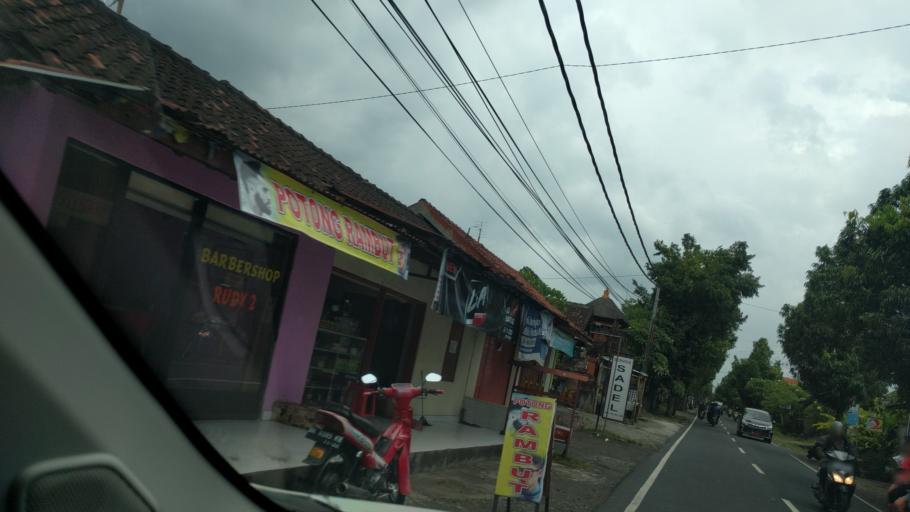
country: ID
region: Bali
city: Banjar Pande
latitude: -8.5138
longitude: 115.2404
